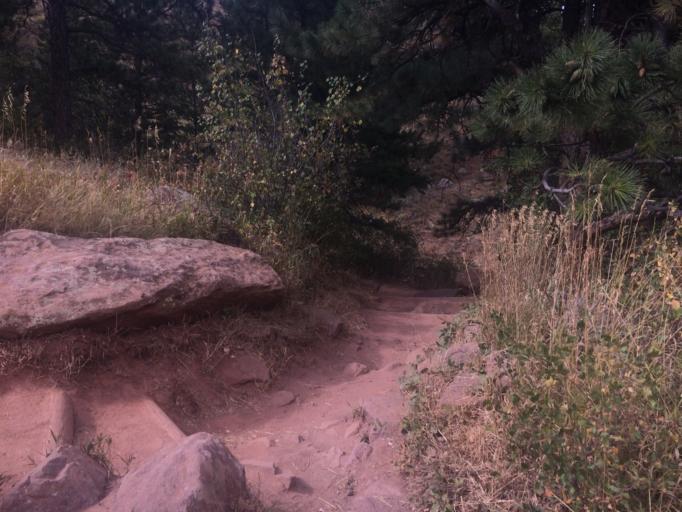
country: US
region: Colorado
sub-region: Boulder County
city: Boulder
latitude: 39.9792
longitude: -105.2838
